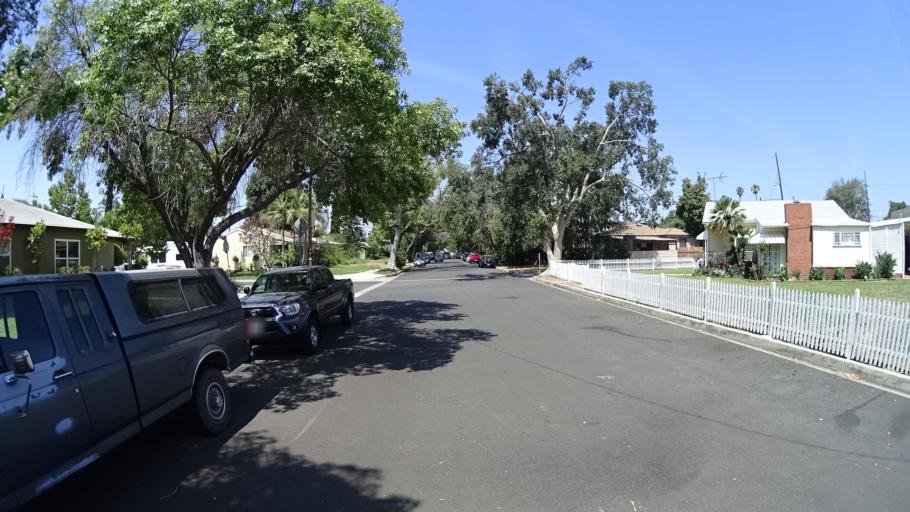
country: US
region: California
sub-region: Los Angeles County
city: Van Nuys
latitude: 34.2075
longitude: -118.4528
